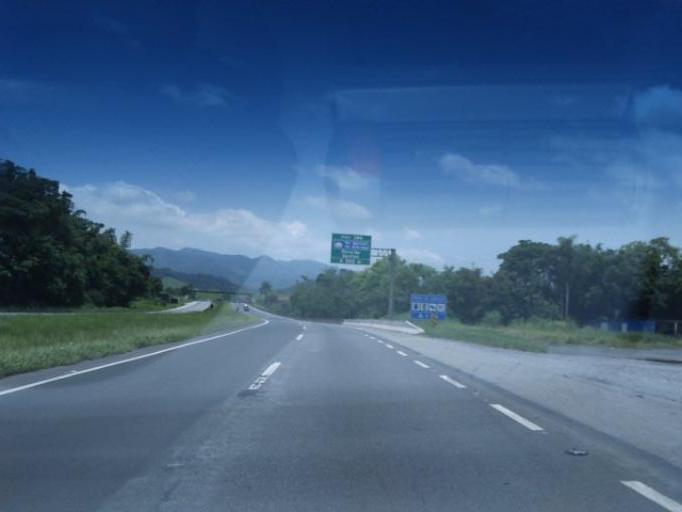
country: BR
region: Sao Paulo
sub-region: Miracatu
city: Miracatu
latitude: -24.2474
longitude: -47.3699
